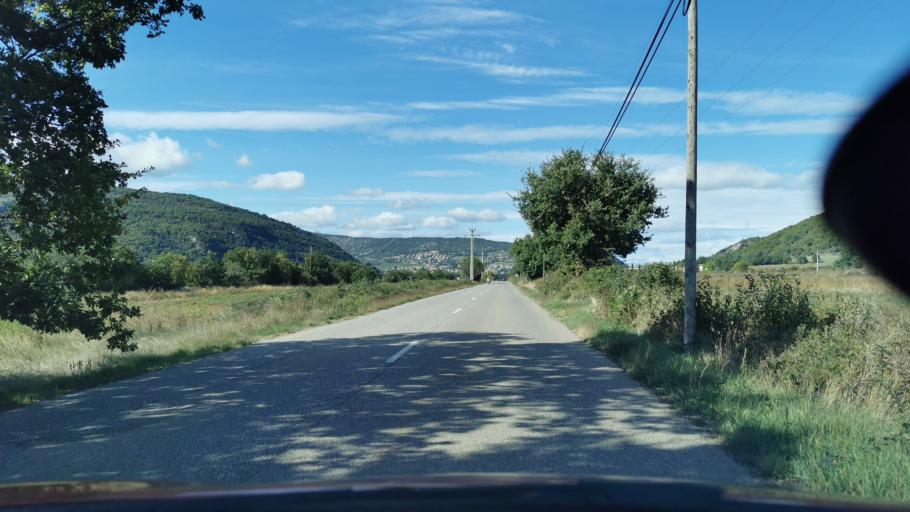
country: FR
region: Provence-Alpes-Cote d'Azur
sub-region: Departement des Alpes-de-Haute-Provence
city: Peipin
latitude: 44.1630
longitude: 5.9636
